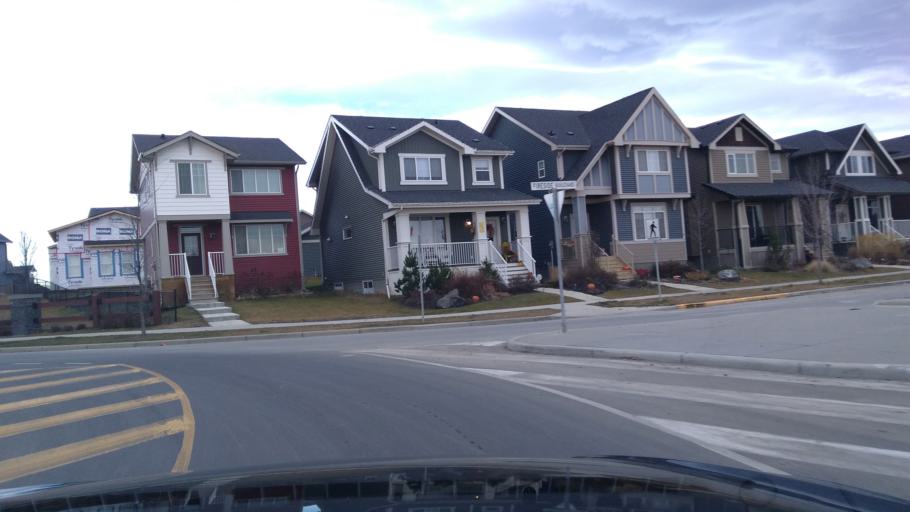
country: CA
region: Alberta
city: Cochrane
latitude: 51.1584
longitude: -114.4745
